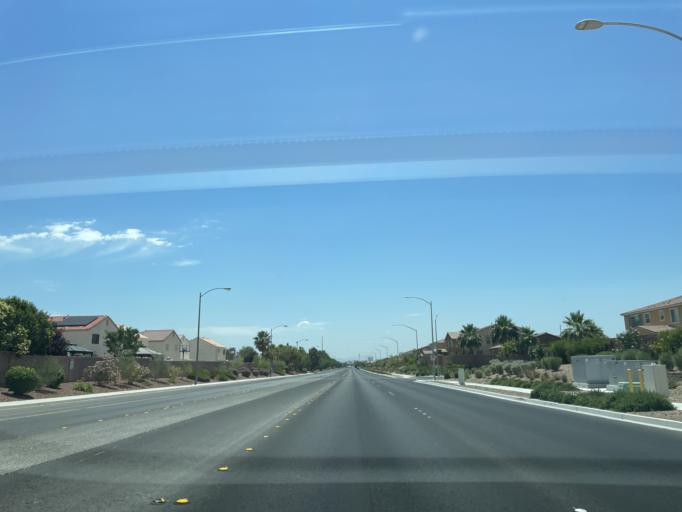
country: US
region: Nevada
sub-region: Clark County
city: North Las Vegas
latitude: 36.2820
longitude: -115.1532
